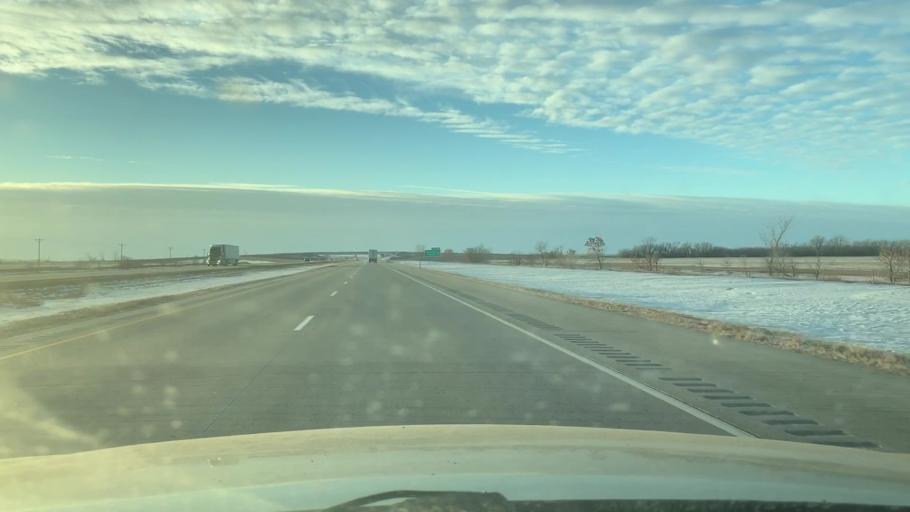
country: US
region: North Dakota
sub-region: Cass County
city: Casselton
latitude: 46.8758
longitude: -97.3350
